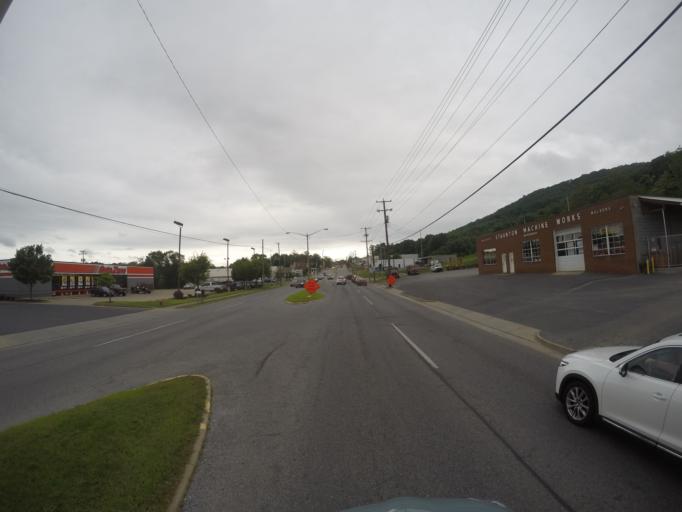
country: US
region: Virginia
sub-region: City of Staunton
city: Staunton
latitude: 38.1438
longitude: -79.0578
